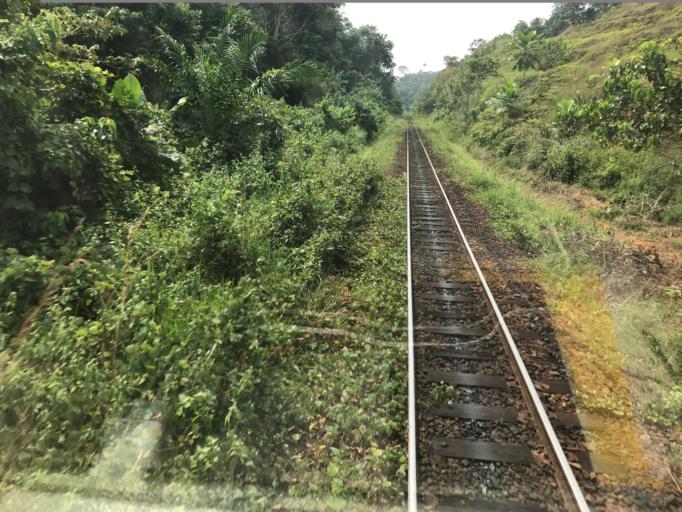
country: CM
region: Centre
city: Eseka
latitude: 3.5781
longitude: 10.8906
